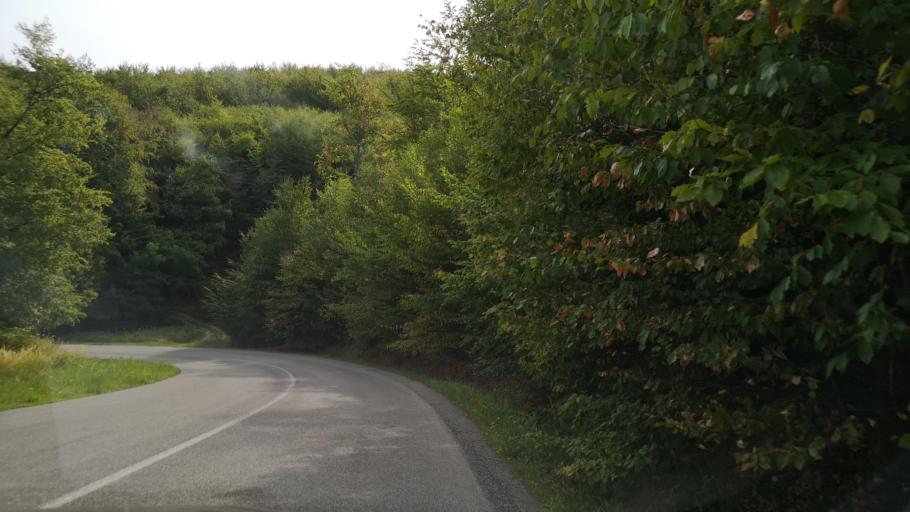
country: SK
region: Banskobystricky
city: Tisovec
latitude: 48.5790
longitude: 19.9987
